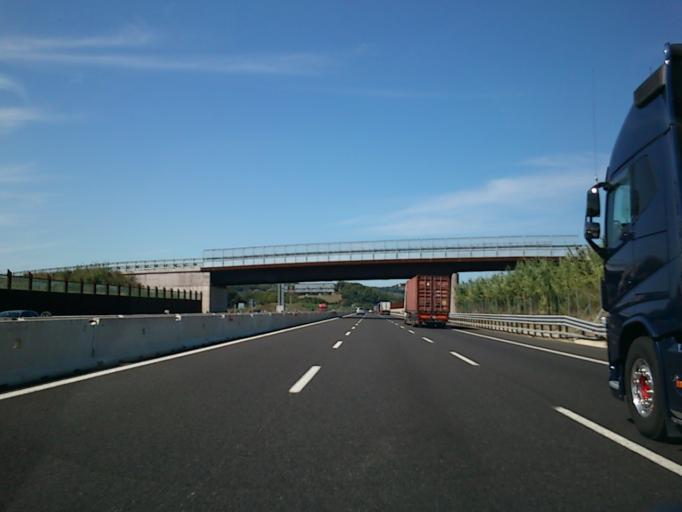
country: IT
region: The Marches
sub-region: Provincia di Pesaro e Urbino
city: Centinarola
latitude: 43.8405
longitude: 12.9812
